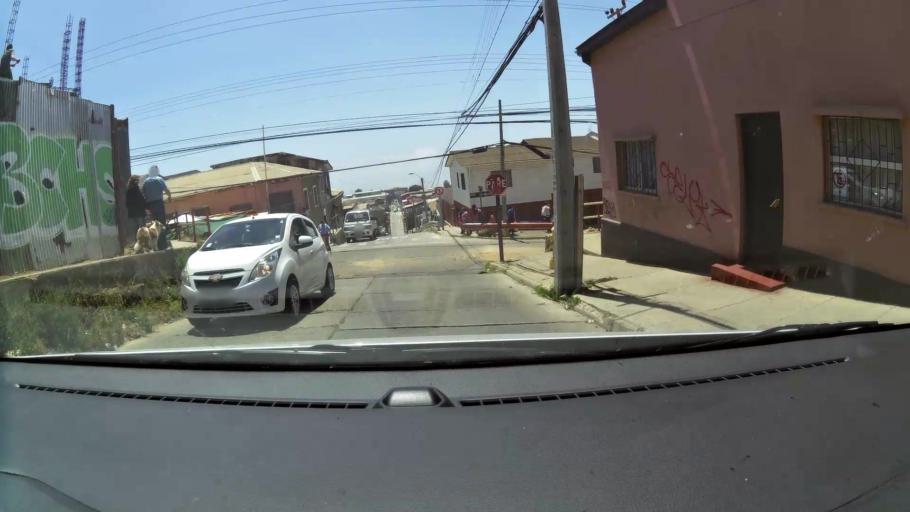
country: CL
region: Valparaiso
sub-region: Provincia de Valparaiso
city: Valparaiso
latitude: -33.0342
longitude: -71.6401
